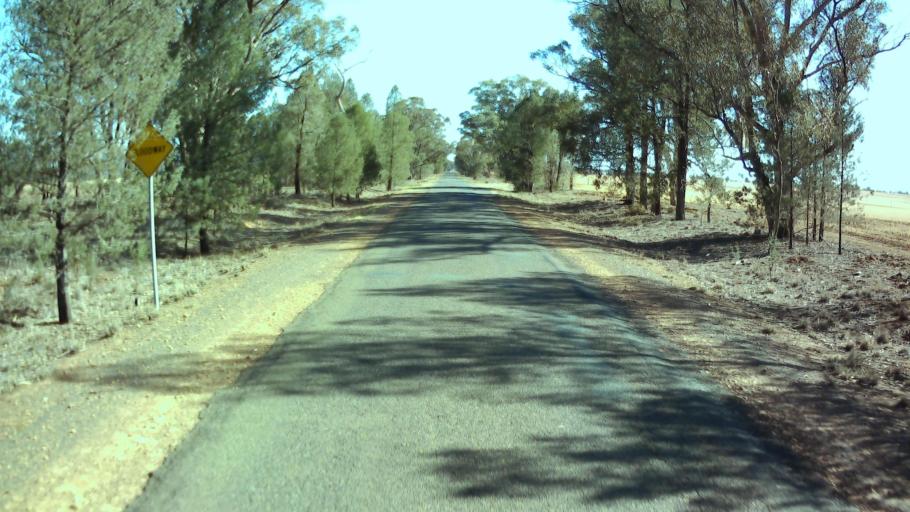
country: AU
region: New South Wales
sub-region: Weddin
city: Grenfell
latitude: -33.8080
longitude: 147.9545
